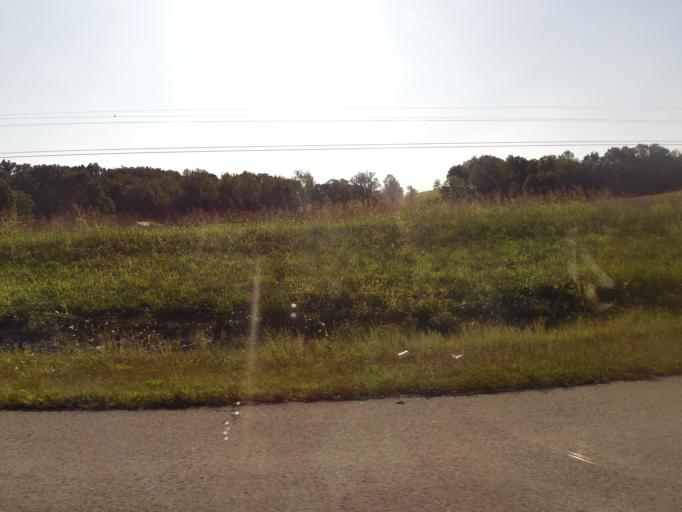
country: US
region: Tennessee
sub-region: Claiborne County
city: Tazewell
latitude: 36.5011
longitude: -83.5944
